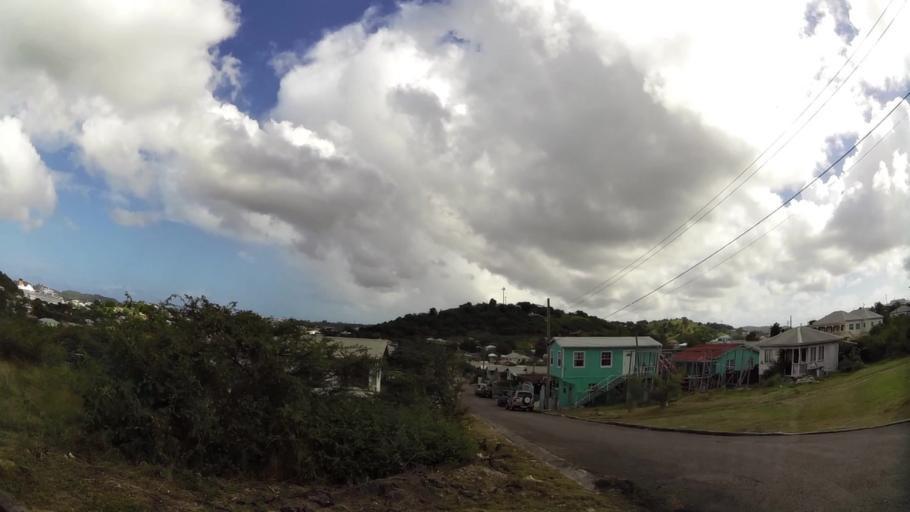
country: AG
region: Saint John
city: Saint John's
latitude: 17.1109
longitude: -61.8565
